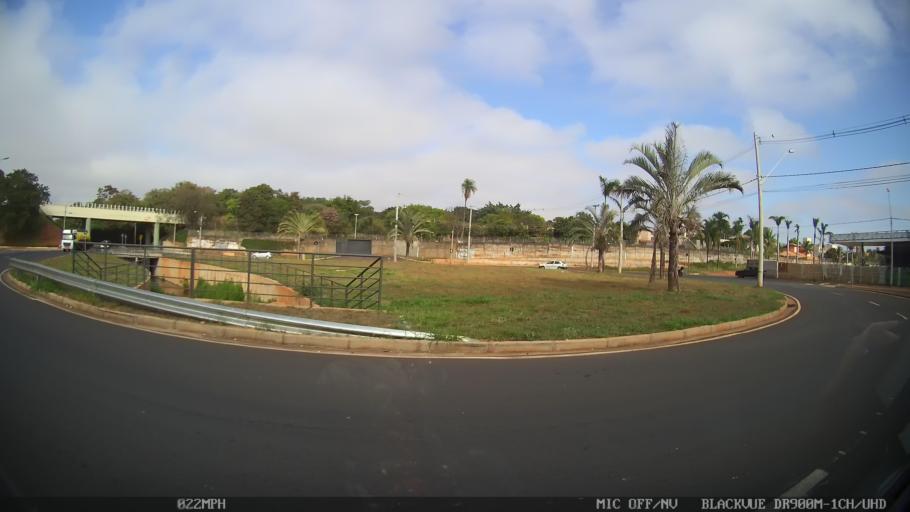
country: BR
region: Sao Paulo
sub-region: Sao Jose Do Rio Preto
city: Sao Jose do Rio Preto
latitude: -20.8134
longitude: -49.4340
